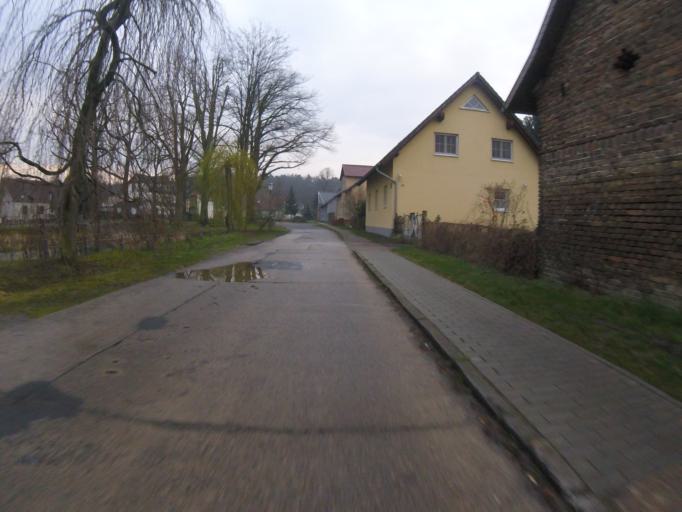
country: DE
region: Brandenburg
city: Konigs Wusterhausen
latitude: 52.2874
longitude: 13.6657
